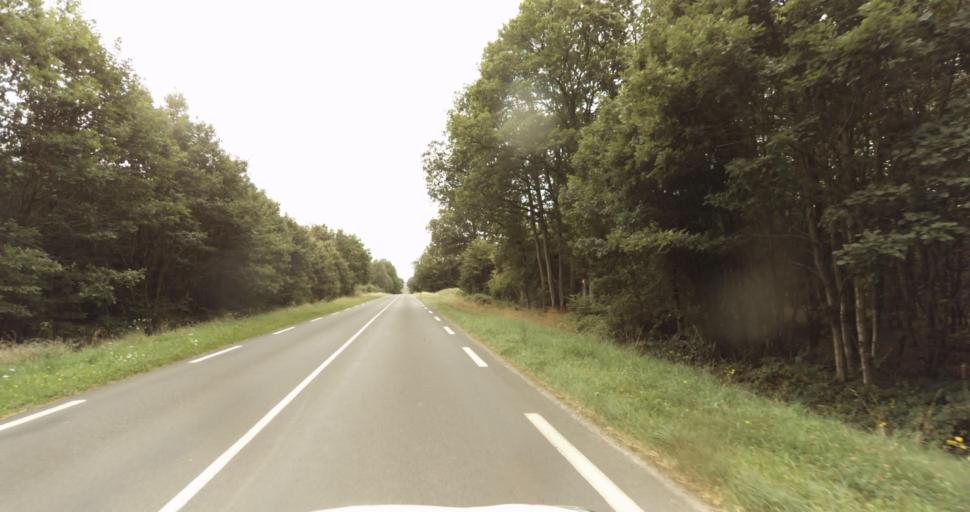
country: FR
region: Haute-Normandie
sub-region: Departement de l'Eure
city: La Madeleine-de-Nonancourt
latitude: 48.8188
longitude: 1.1866
